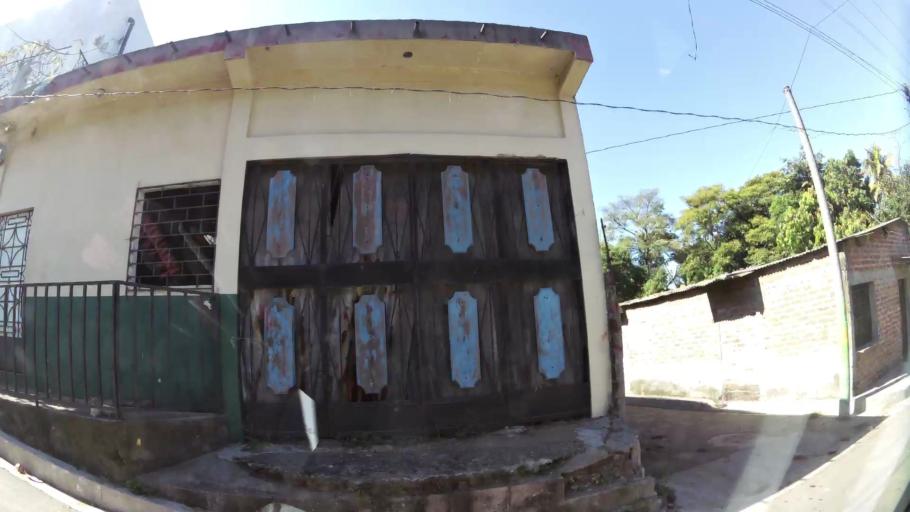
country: SV
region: Sonsonate
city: Armenia
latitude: 13.7328
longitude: -89.3827
